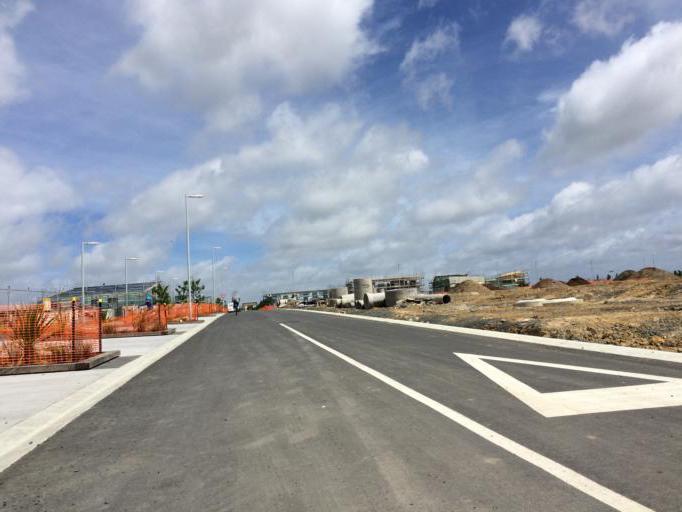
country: NZ
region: Auckland
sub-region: Auckland
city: North Shore
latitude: -36.7947
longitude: 174.6703
